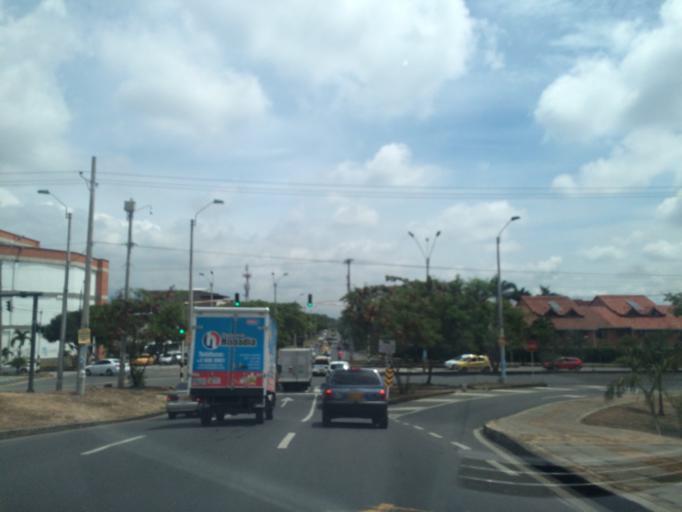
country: CO
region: Valle del Cauca
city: Cali
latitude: 3.3874
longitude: -76.5283
